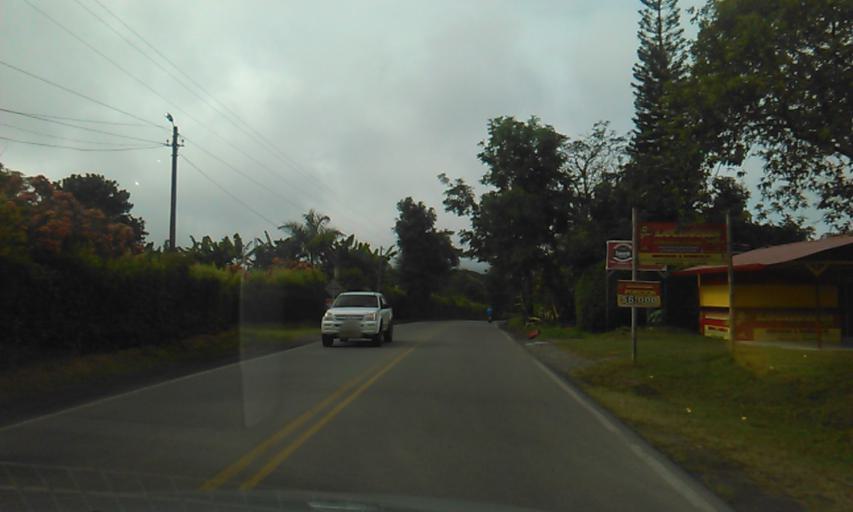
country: CO
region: Quindio
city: Cordoba
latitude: 4.4192
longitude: -75.7228
